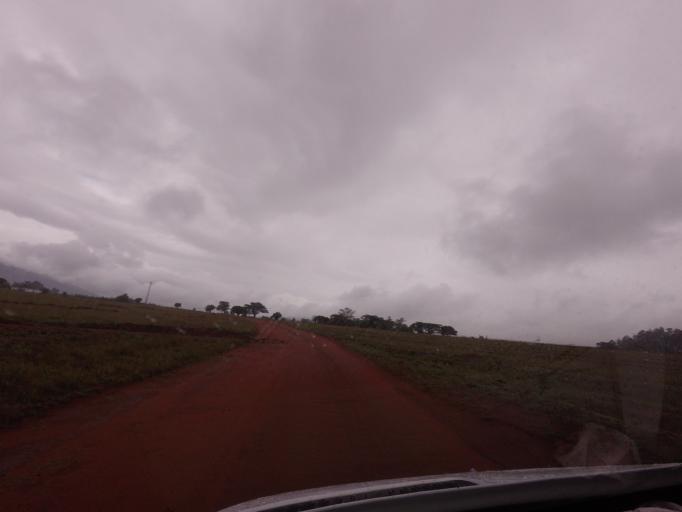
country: SZ
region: Hhohho
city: Lobamba
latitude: -26.4788
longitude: 31.1923
